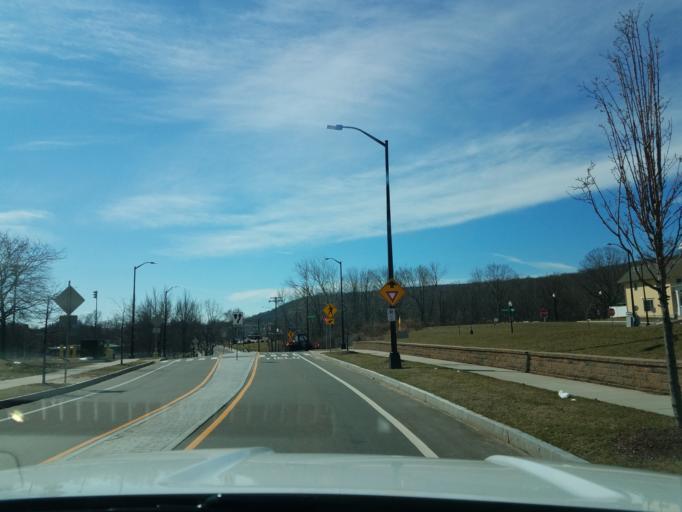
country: US
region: Connecticut
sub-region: New Haven County
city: New Haven
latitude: 41.3478
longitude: -72.9582
